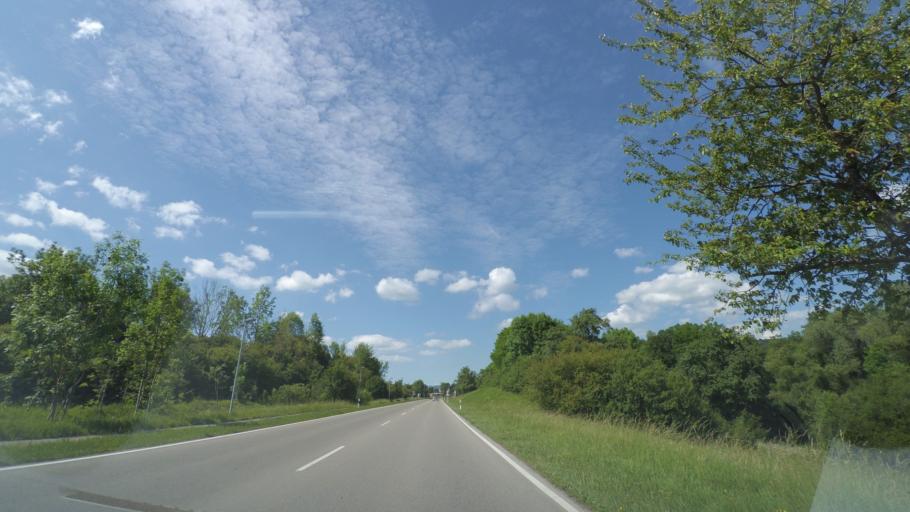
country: DE
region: Baden-Wuerttemberg
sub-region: Regierungsbezirk Stuttgart
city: Gaildorf
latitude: 48.9917
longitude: 9.7742
